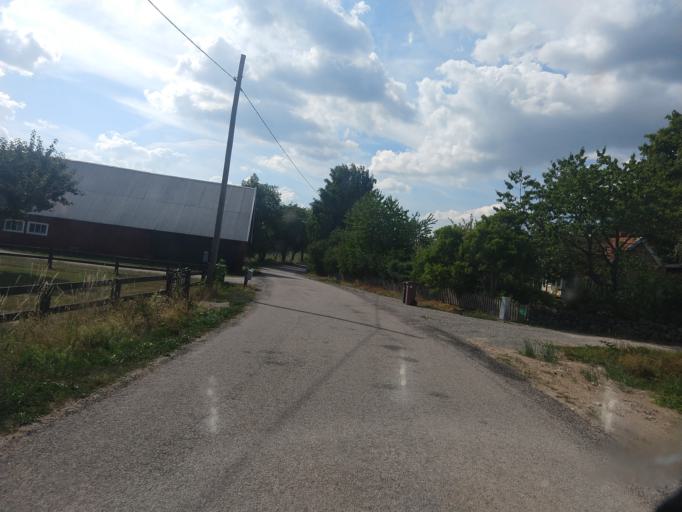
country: SE
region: Blekinge
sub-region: Karlskrona Kommun
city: Nattraby
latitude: 56.2487
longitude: 15.5333
